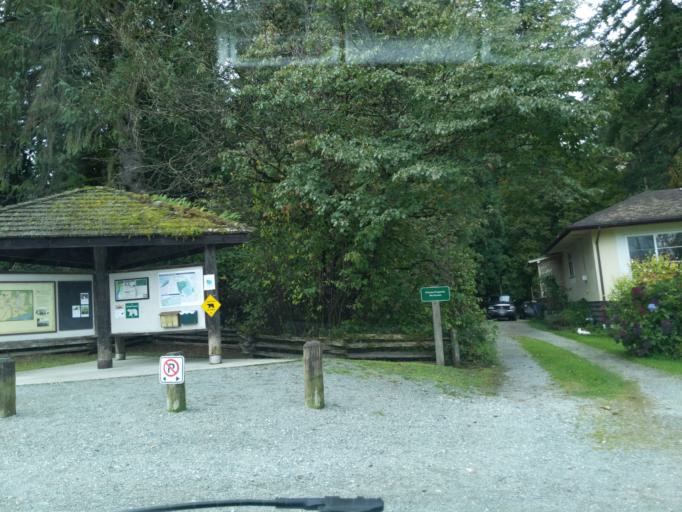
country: CA
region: British Columbia
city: Maple Ridge
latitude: 49.1983
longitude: -122.5948
